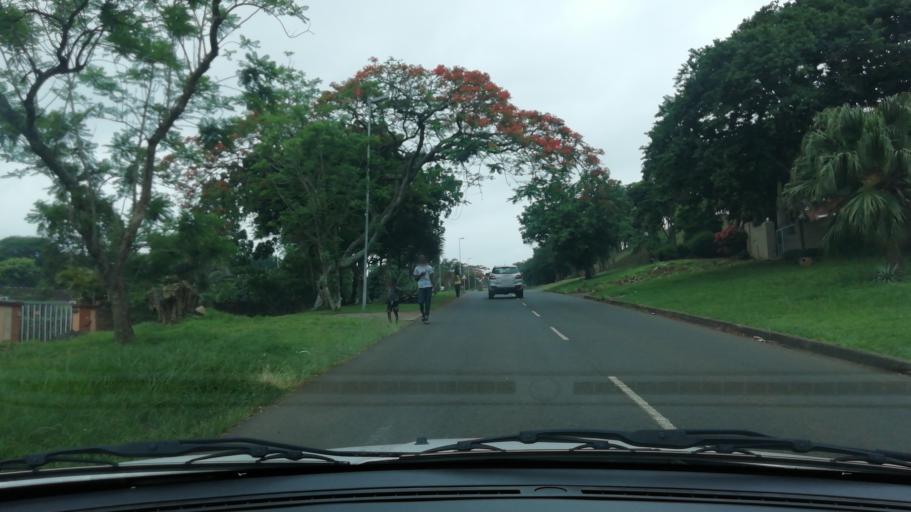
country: ZA
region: KwaZulu-Natal
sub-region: uThungulu District Municipality
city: Empangeni
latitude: -28.7556
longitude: 31.8841
